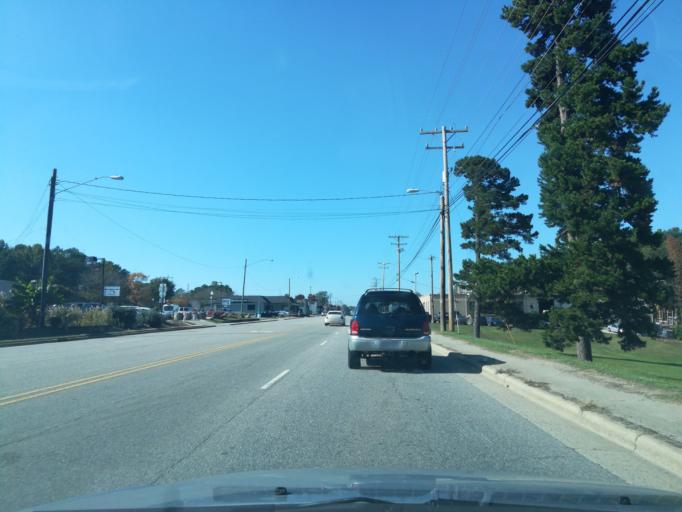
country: US
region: North Carolina
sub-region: Durham County
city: Durham
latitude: 36.0166
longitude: -78.9386
